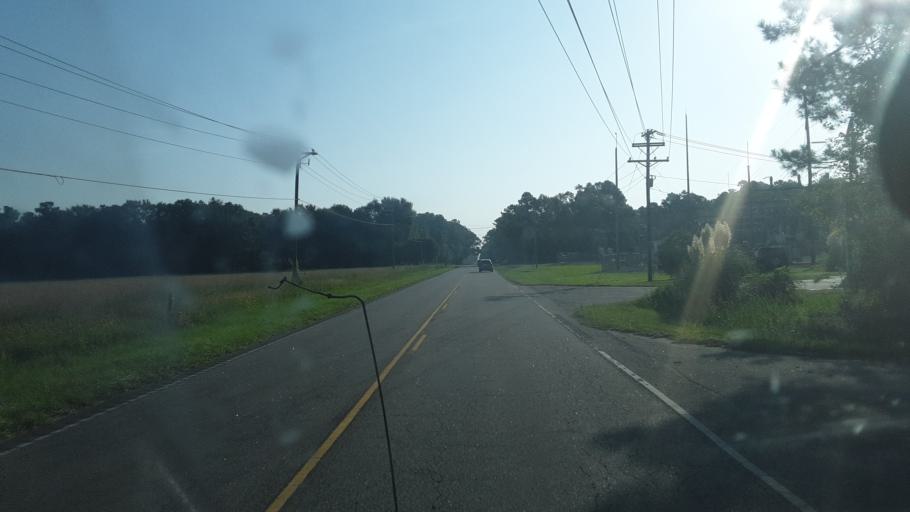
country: US
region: South Carolina
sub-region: Horry County
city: Forestbrook
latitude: 33.8366
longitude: -78.8779
